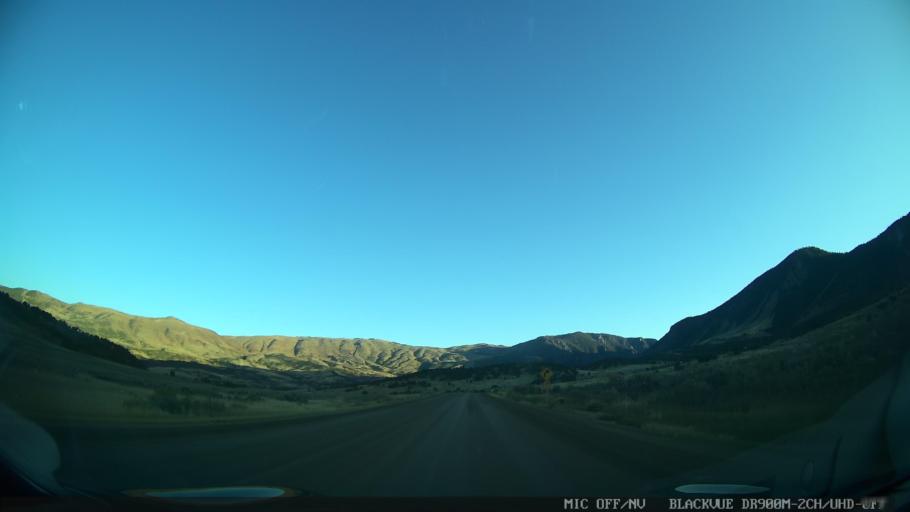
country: US
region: Colorado
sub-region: Grand County
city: Kremmling
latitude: 39.9706
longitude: -106.5025
